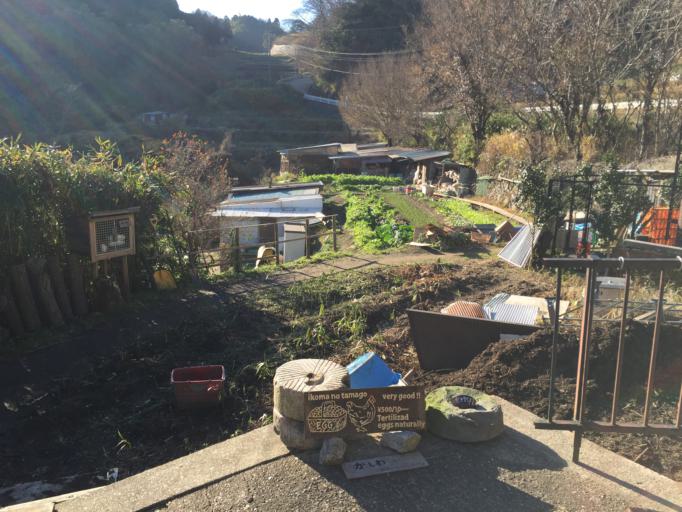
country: JP
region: Nara
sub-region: Ikoma-shi
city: Ikoma
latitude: 34.6667
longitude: 135.6762
